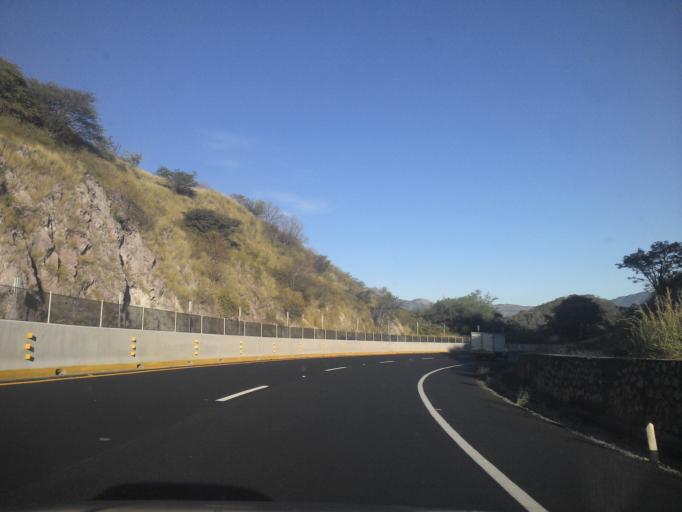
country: MX
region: Jalisco
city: Hostotipaquillo
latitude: 21.0189
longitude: -104.1978
